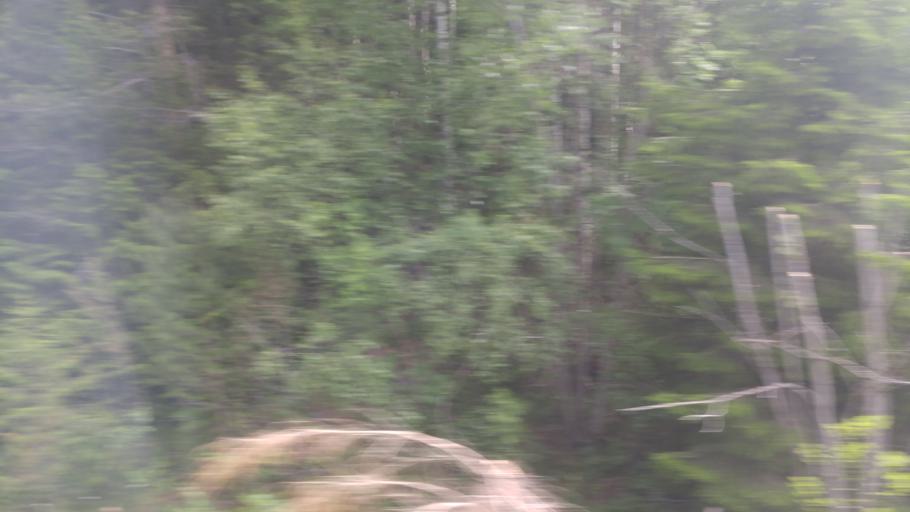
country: NO
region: Sor-Trondelag
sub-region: Midtre Gauldal
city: Storen
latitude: 62.9998
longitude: 10.4681
